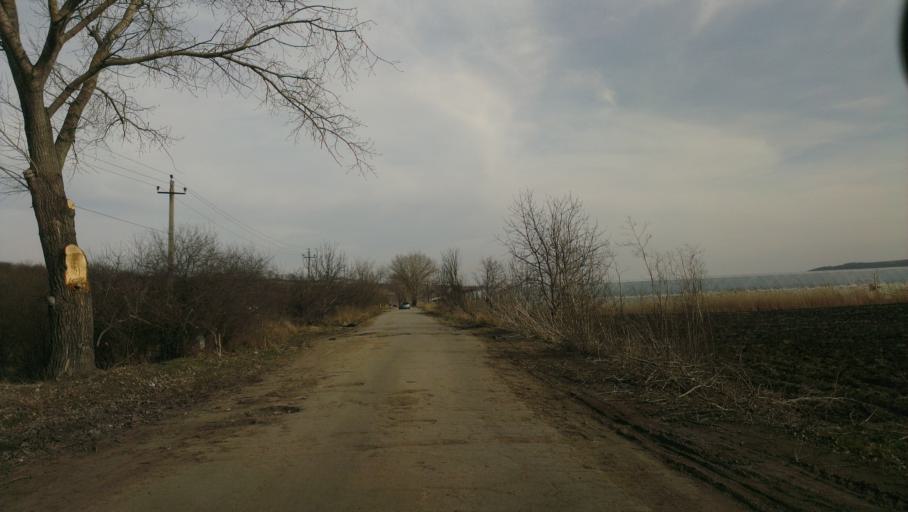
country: MD
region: Laloveni
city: Ialoveni
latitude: 46.9162
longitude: 28.6911
